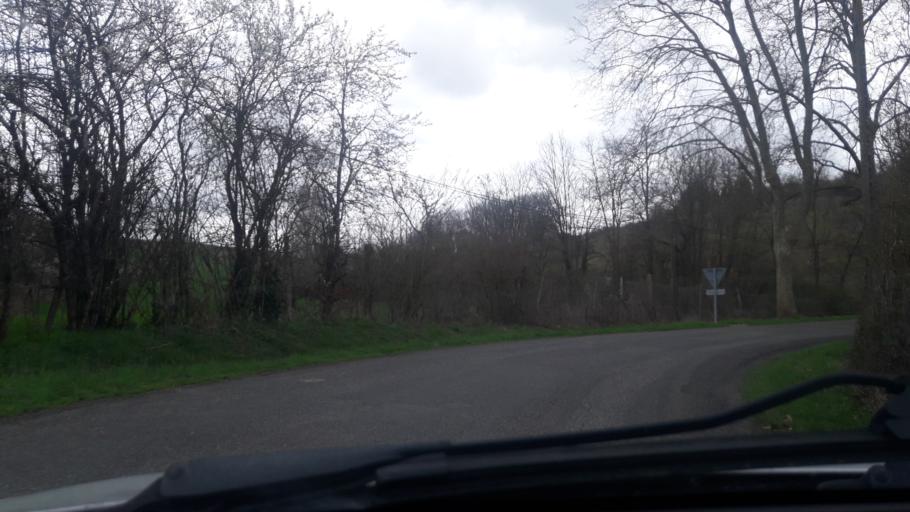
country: FR
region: Midi-Pyrenees
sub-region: Departement de la Haute-Garonne
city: Montesquieu-Volvestre
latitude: 43.2314
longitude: 1.2860
